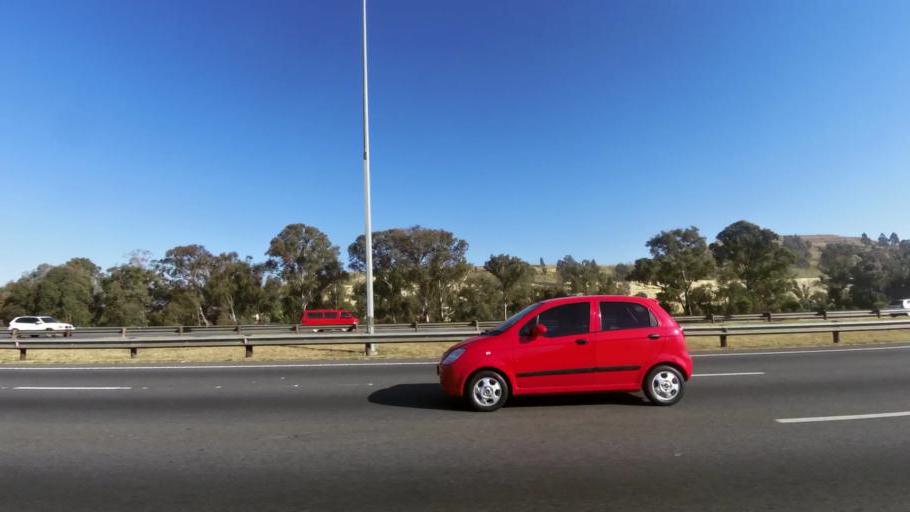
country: ZA
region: Gauteng
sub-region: City of Johannesburg Metropolitan Municipality
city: Johannesburg
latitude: -26.2306
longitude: 27.9611
